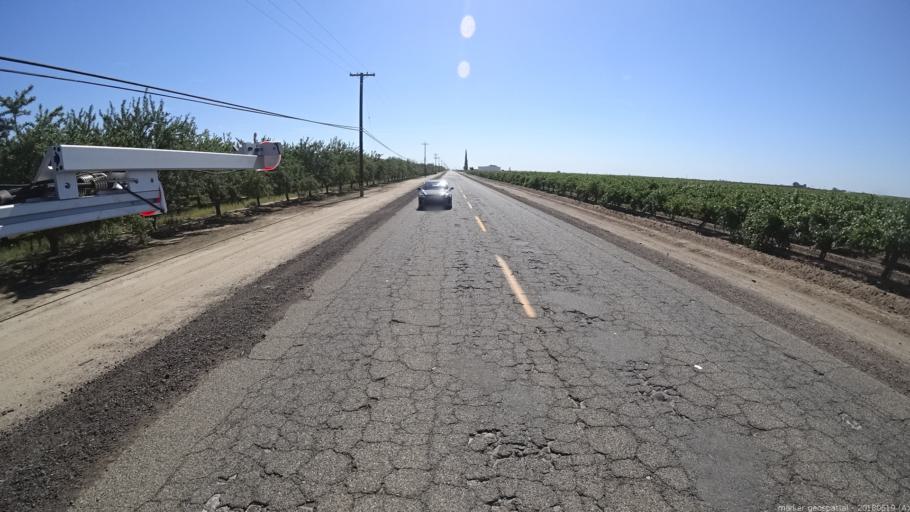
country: US
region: California
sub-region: Fresno County
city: Biola
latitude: 36.8367
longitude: -120.1494
